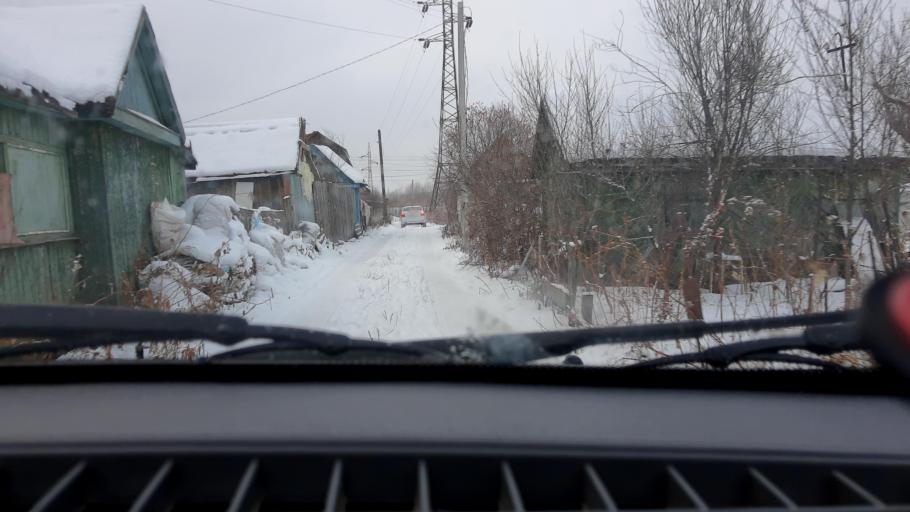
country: RU
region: Bashkortostan
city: Ufa
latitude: 54.8259
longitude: 56.1264
